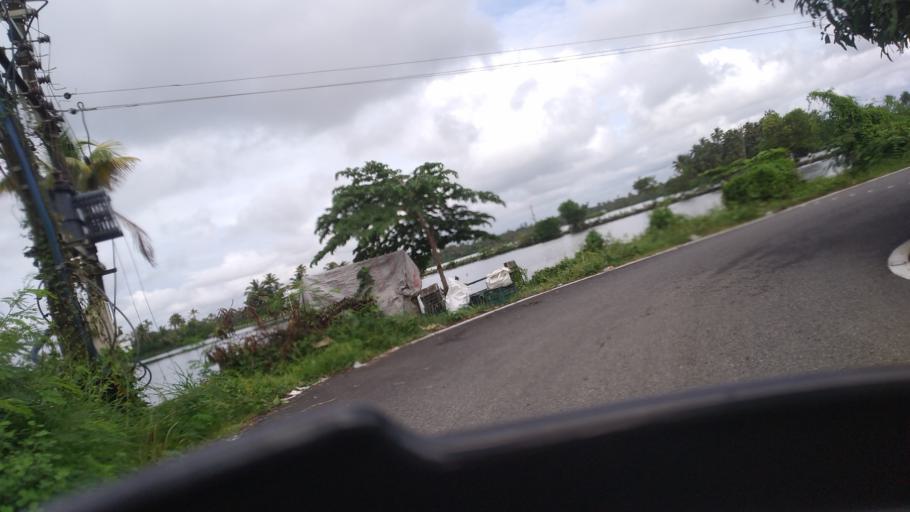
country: IN
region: Kerala
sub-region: Ernakulam
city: Elur
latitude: 10.0968
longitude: 76.1909
